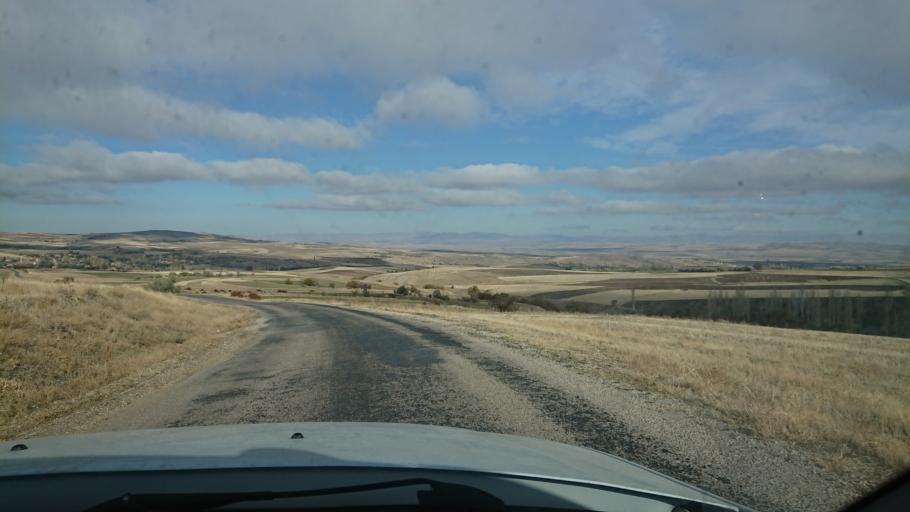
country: TR
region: Aksaray
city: Ortakoy
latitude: 38.7933
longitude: 33.9967
